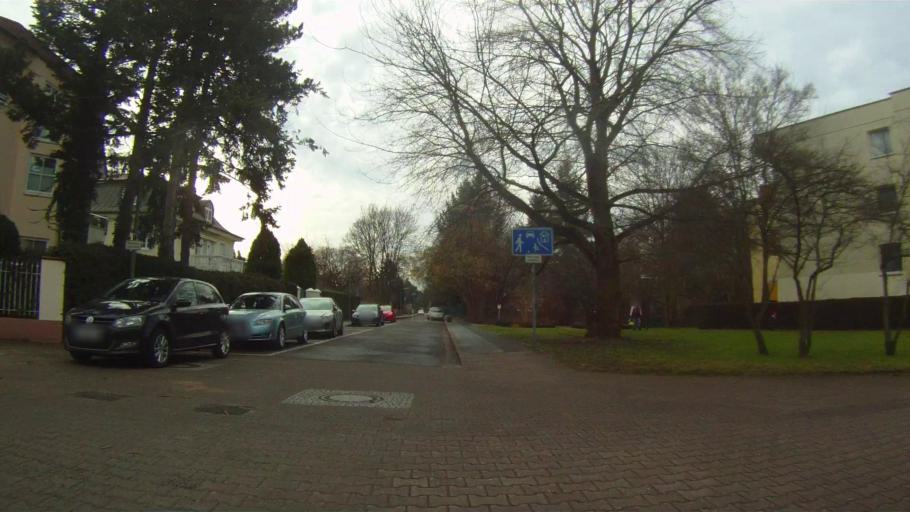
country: DE
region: Berlin
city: Mariendorf
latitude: 52.4320
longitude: 13.3987
